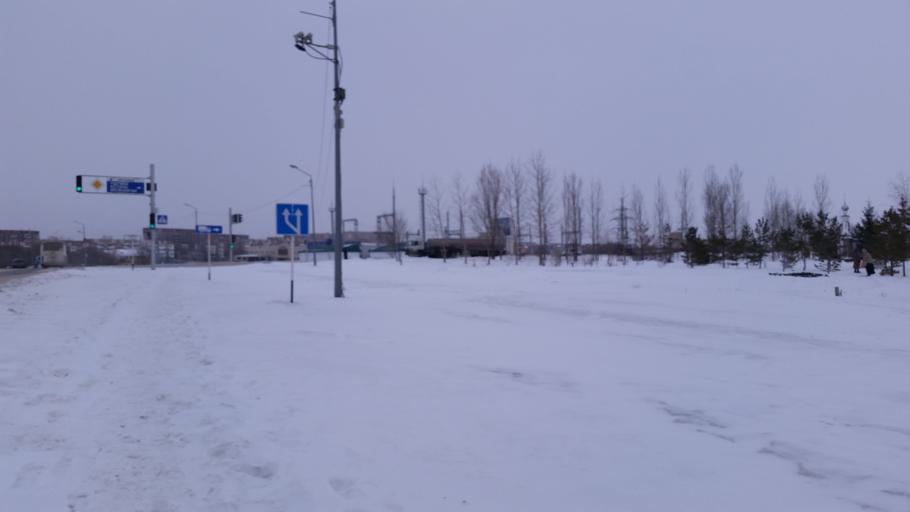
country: KZ
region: Qaraghandy
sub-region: Qaraghandy Qalasy
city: Karagandy
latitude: 49.7746
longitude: 73.1563
